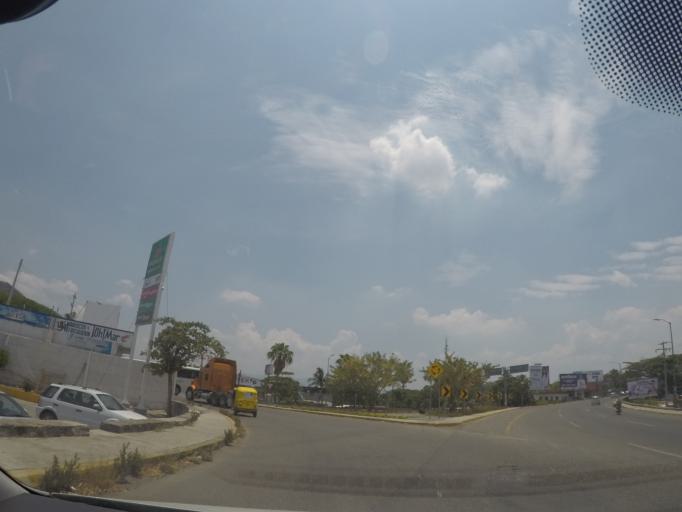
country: MX
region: Oaxaca
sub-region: Santo Domingo Tehuantepec
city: Santo Domingo Tehuantepec
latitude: 16.3241
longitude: -95.2397
